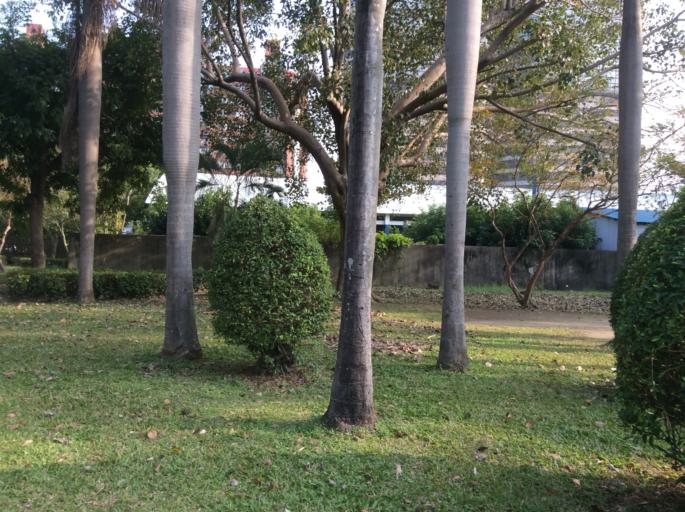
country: TW
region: Kaohsiung
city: Kaohsiung
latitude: 22.6066
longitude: 120.3089
